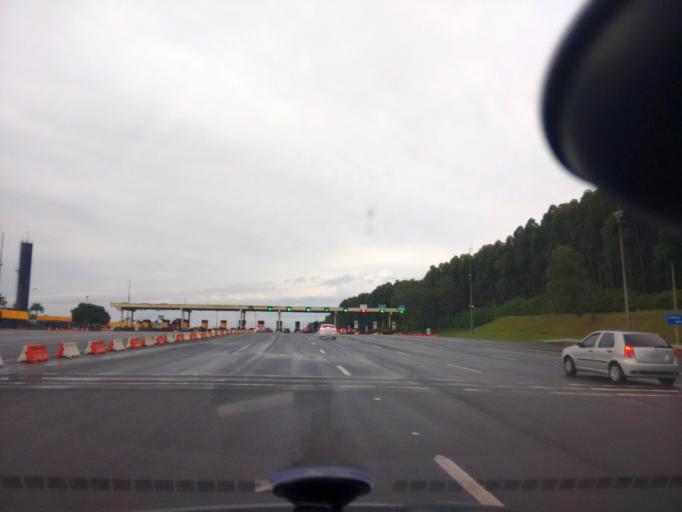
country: BR
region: Sao Paulo
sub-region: Itirapina
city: Itirapina
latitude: -22.1302
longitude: -47.8071
